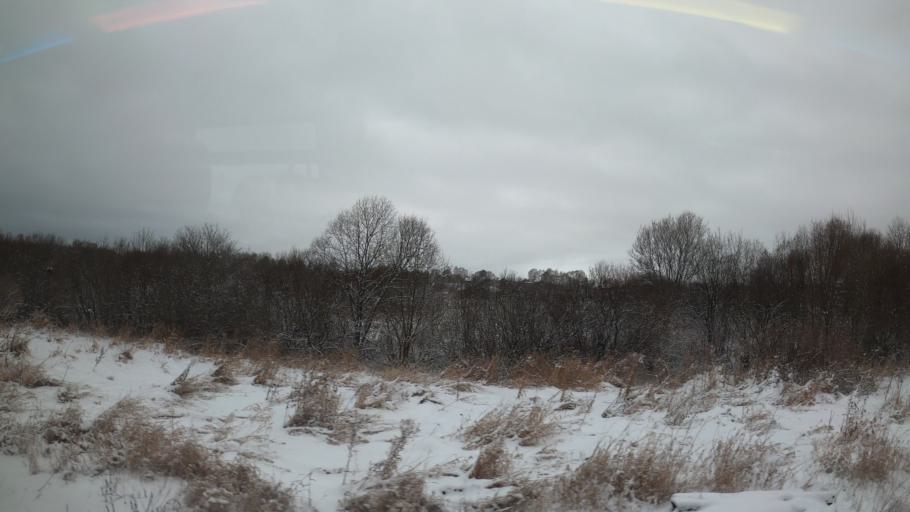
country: RU
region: Jaroslavl
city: Pereslavl'-Zalesskiy
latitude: 56.7062
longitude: 38.9099
